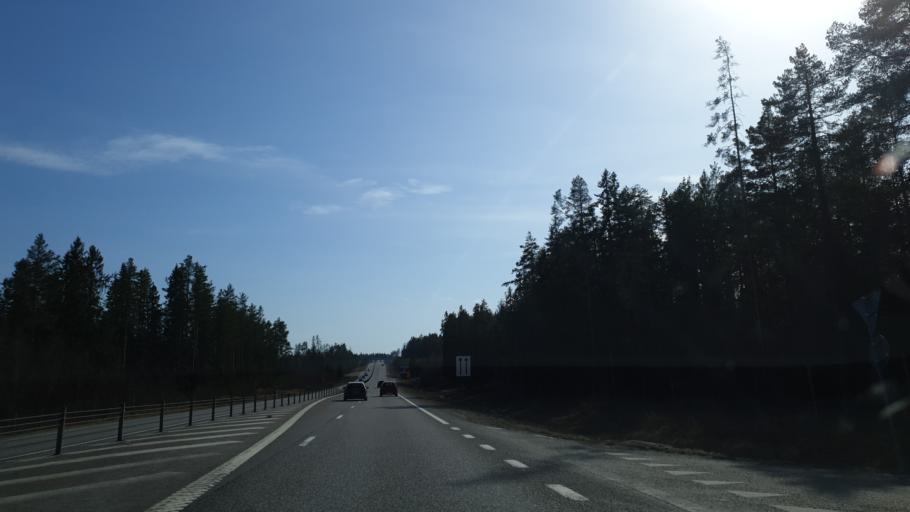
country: SE
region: Vaesternorrland
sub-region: Sundsvalls Kommun
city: Njurundabommen
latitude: 62.1053
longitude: 17.3139
